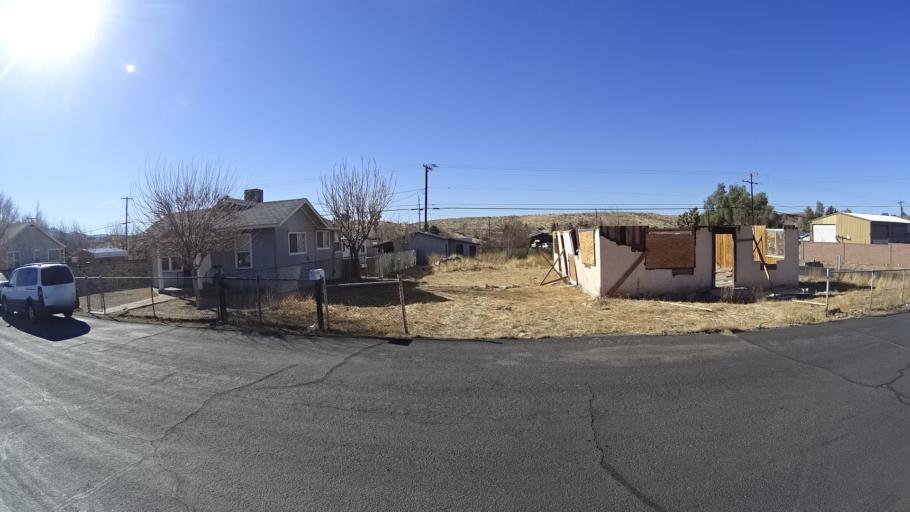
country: US
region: Arizona
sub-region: Mohave County
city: Kingman
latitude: 35.1871
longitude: -114.0487
